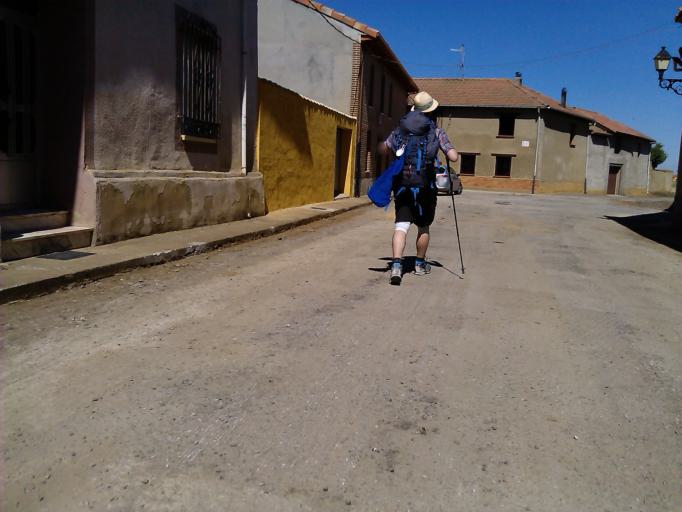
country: ES
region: Castille and Leon
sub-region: Provincia de Leon
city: Vallecillo
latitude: 42.4230
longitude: -5.2222
